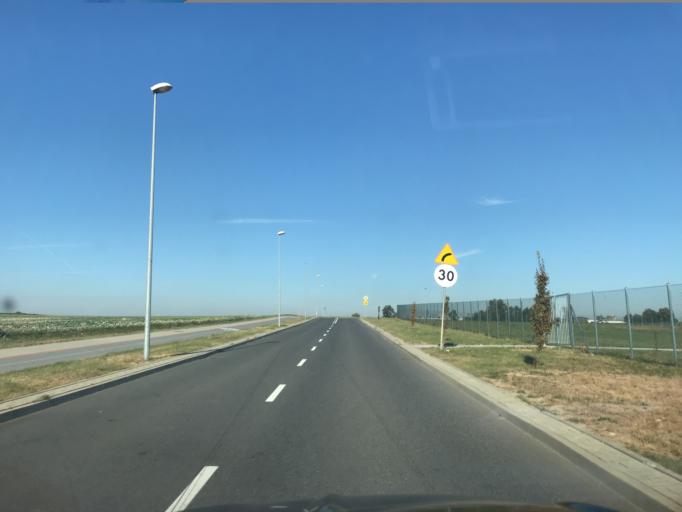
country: PL
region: Warmian-Masurian Voivodeship
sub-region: Powiat ilawski
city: Lubawa
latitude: 53.5143
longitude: 19.7254
